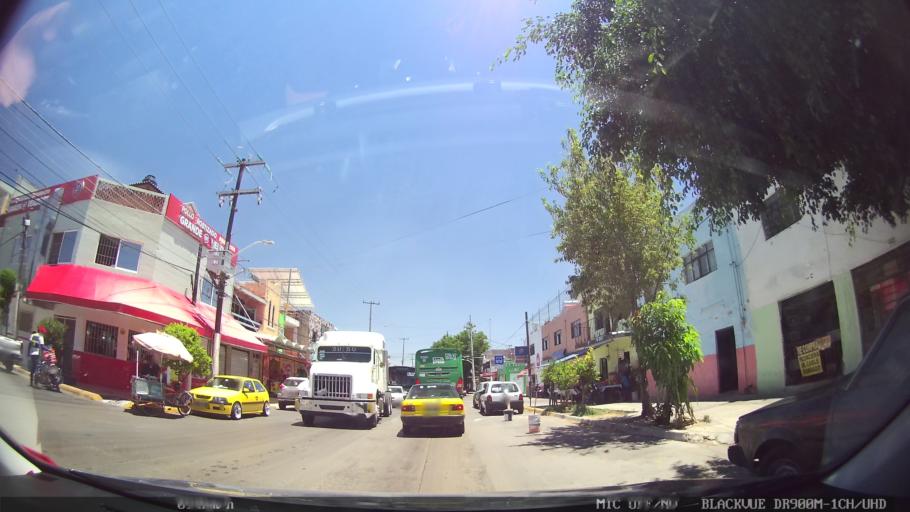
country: MX
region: Jalisco
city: Tlaquepaque
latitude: 20.6685
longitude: -103.2761
